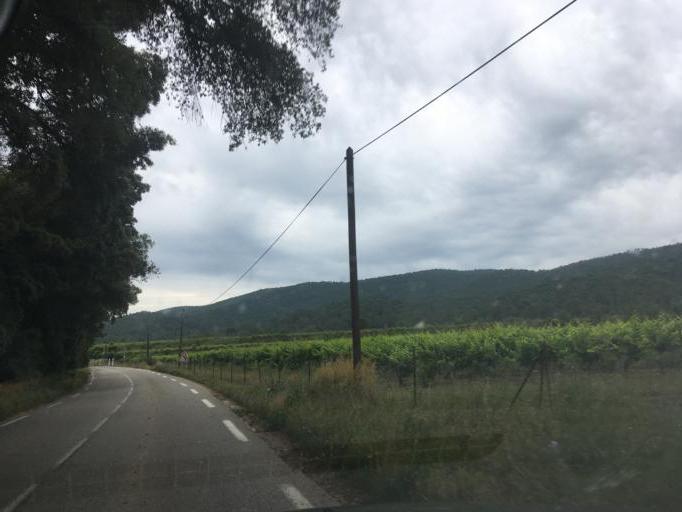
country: FR
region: Provence-Alpes-Cote d'Azur
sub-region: Departement du Var
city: Pierrefeu-du-Var
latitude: 43.2322
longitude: 6.1794
